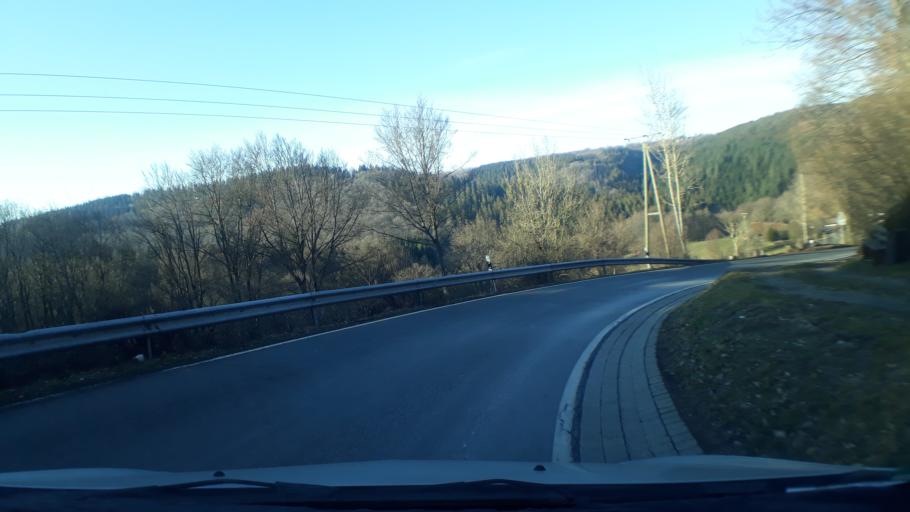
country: DE
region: North Rhine-Westphalia
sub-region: Regierungsbezirk Koln
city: Simmerath
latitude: 50.5586
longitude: 6.2949
